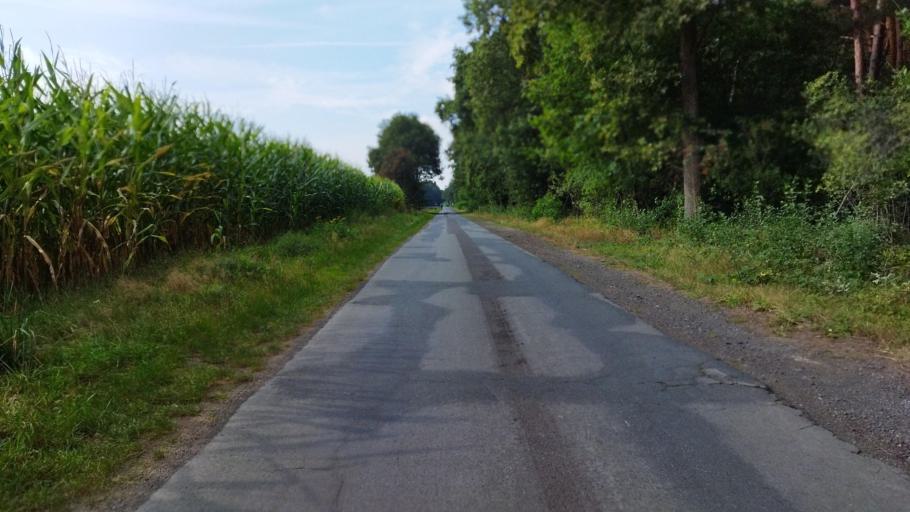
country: DE
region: North Rhine-Westphalia
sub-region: Regierungsbezirk Munster
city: Sassenberg
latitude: 52.0039
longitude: 8.0211
